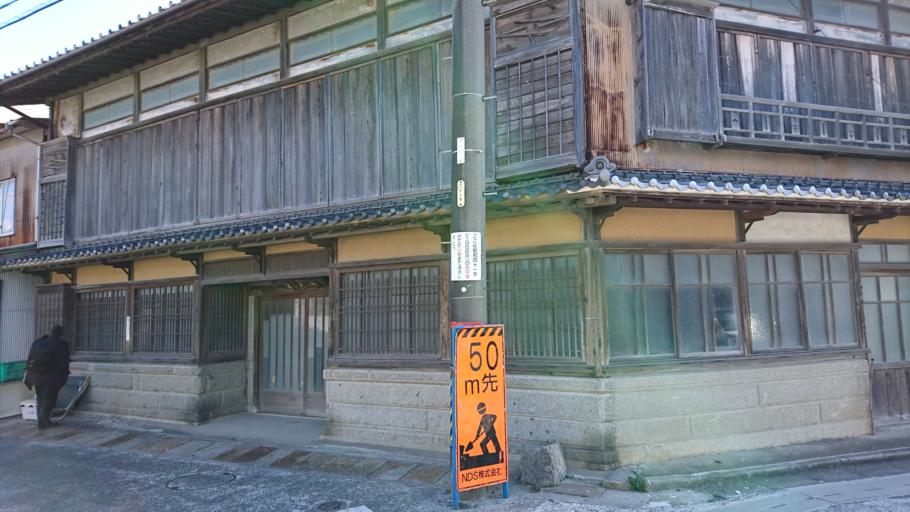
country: JP
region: Aichi
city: Tahara
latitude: 34.6675
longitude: 137.2647
